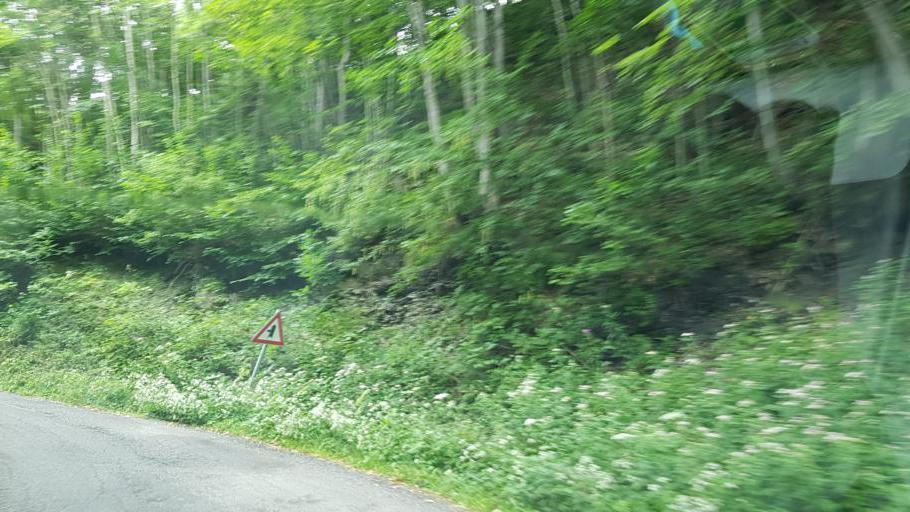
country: IT
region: Piedmont
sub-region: Provincia di Cuneo
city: Stroppo
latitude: 44.5154
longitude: 7.1146
